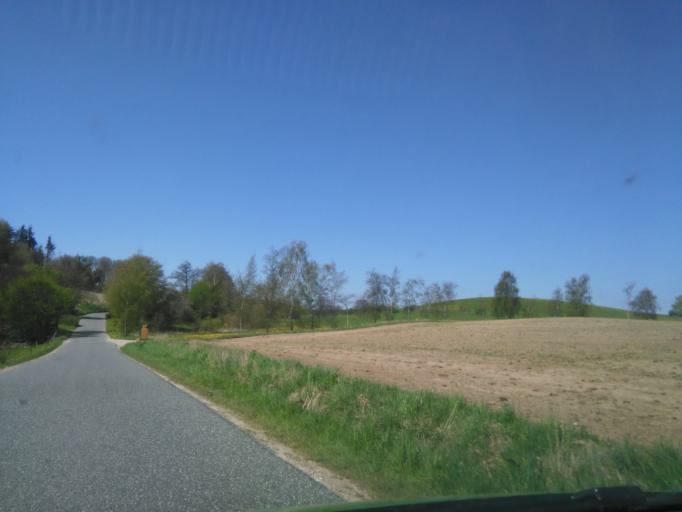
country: DK
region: Central Jutland
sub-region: Odder Kommune
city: Odder
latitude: 55.8985
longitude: 10.0535
